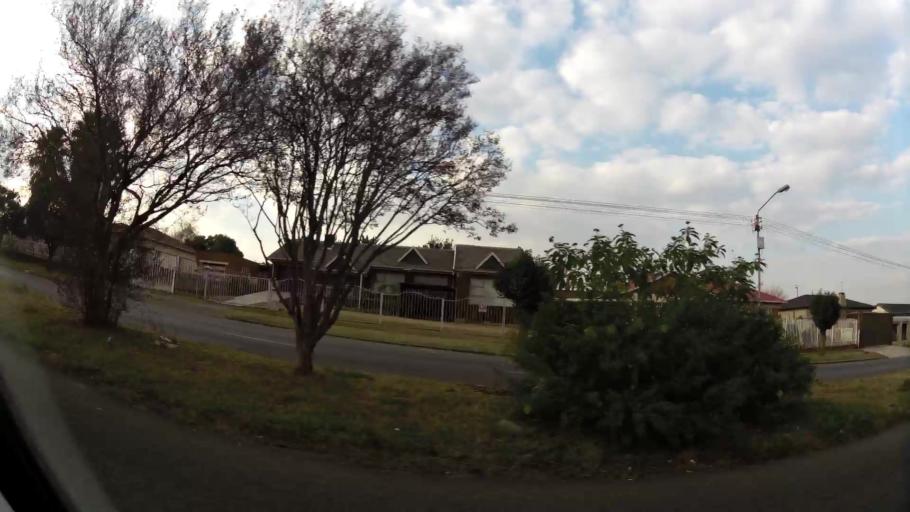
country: ZA
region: Gauteng
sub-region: Ekurhuleni Metropolitan Municipality
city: Germiston
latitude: -26.2443
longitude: 28.1976
